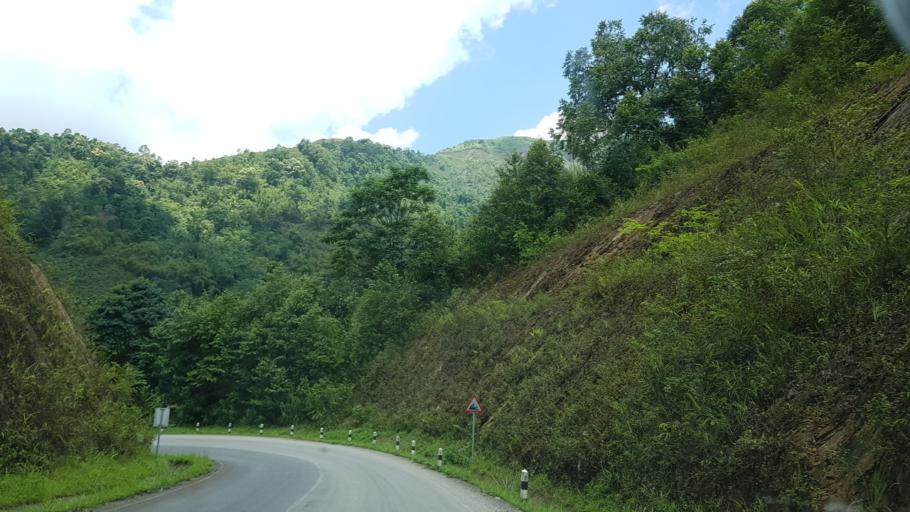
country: LA
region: Vientiane
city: Muang Kasi
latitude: 19.3769
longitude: 102.1578
